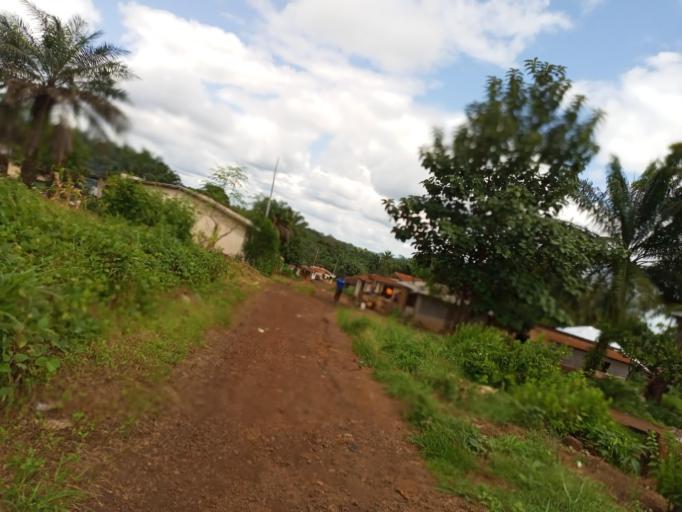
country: SL
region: Northern Province
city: Kamakwie
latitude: 9.4972
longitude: -12.2353
